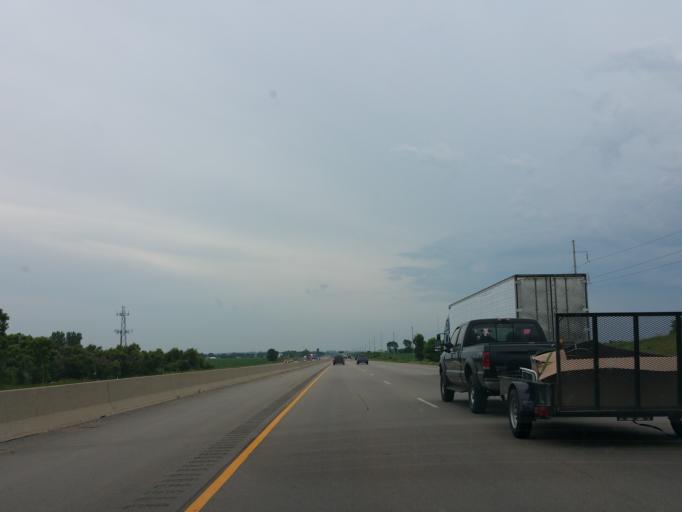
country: US
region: Wisconsin
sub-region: Dane County
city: De Forest
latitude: 43.2315
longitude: -89.3679
